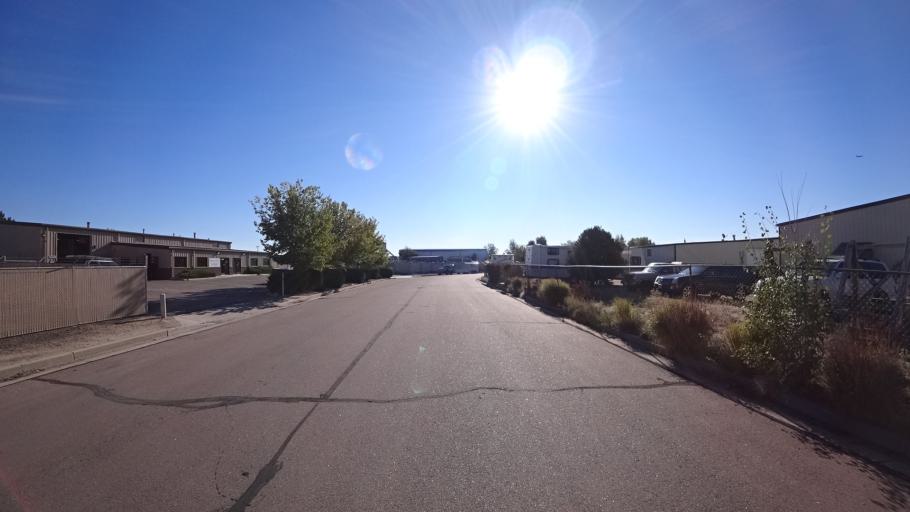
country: US
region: Colorado
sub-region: El Paso County
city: Security-Widefield
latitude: 38.7933
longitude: -104.7234
